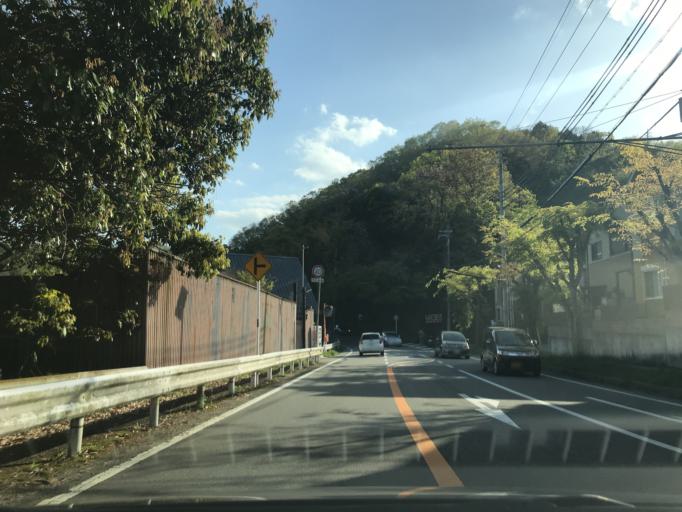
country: JP
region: Hyogo
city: Kawanishi
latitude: 34.8691
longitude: 135.3967
